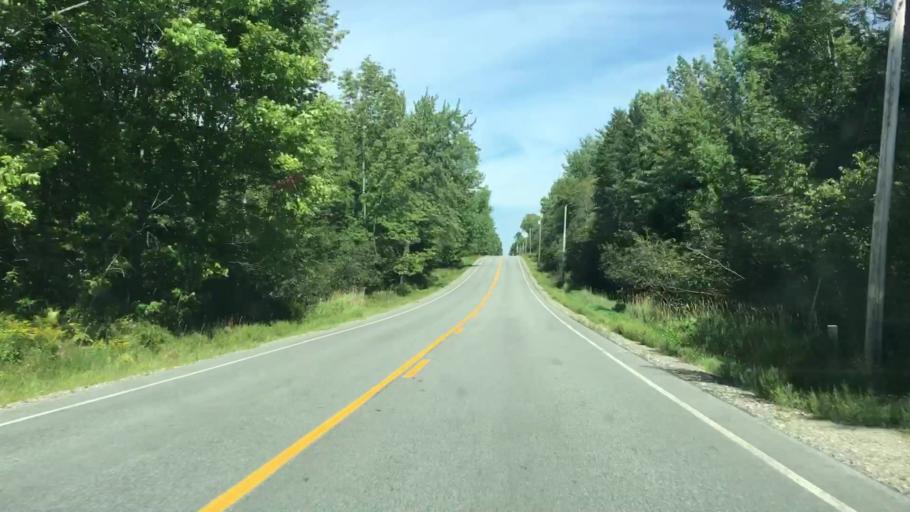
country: US
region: Maine
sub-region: Penobscot County
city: Howland
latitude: 45.2124
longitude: -68.7982
